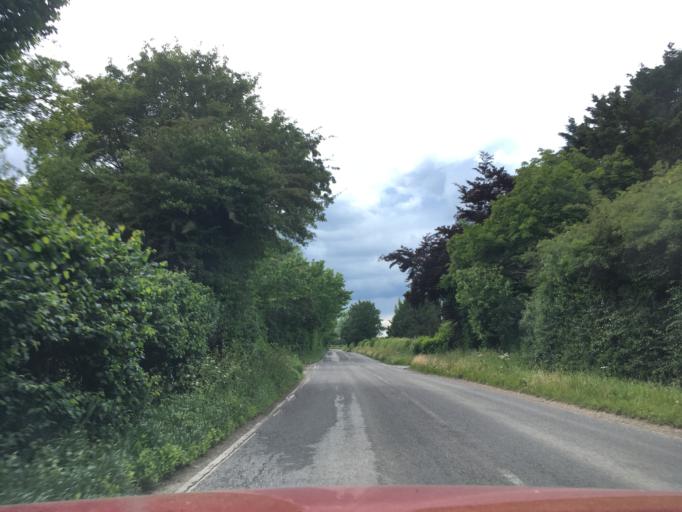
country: GB
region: England
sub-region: Wiltshire
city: Minety
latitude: 51.6559
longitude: -1.9482
